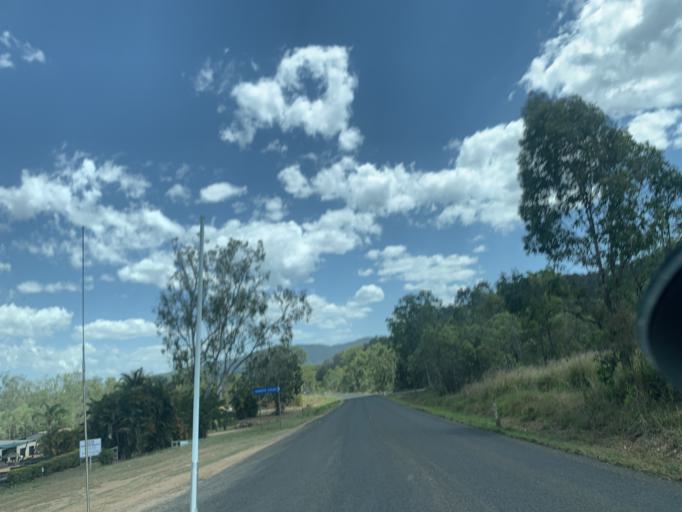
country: AU
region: Queensland
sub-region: Tablelands
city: Atherton
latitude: -17.2926
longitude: 145.4737
